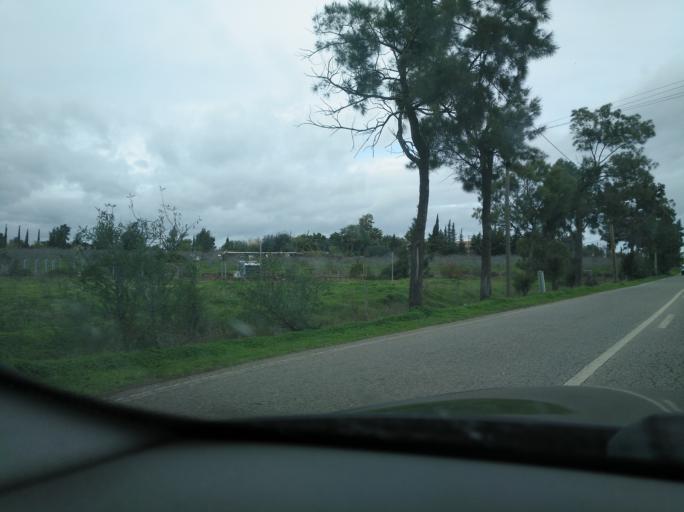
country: PT
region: Faro
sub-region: Vila Real de Santo Antonio
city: Monte Gordo
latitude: 37.1970
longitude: -7.4834
